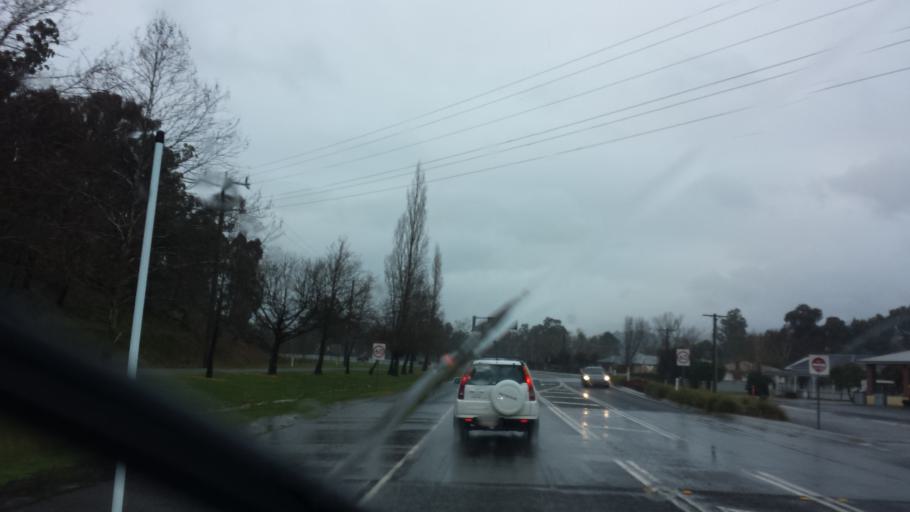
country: AU
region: Victoria
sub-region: Wangaratta
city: Wangaratta
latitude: -36.5682
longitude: 146.7305
